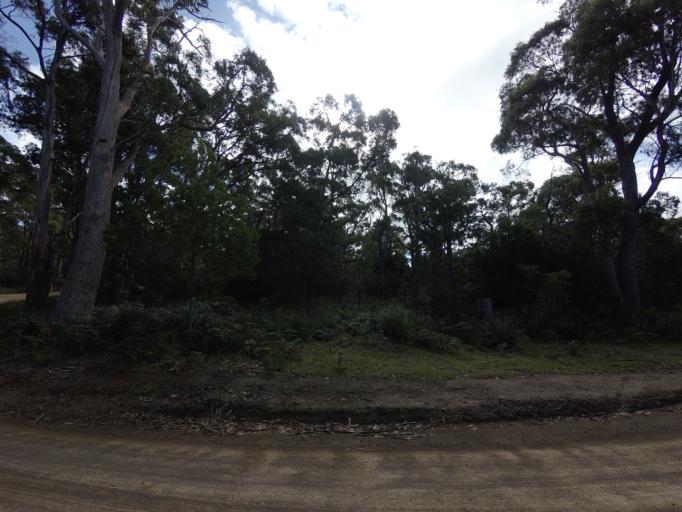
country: AU
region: Tasmania
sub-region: Clarence
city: Sandford
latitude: -43.0928
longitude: 147.7147
